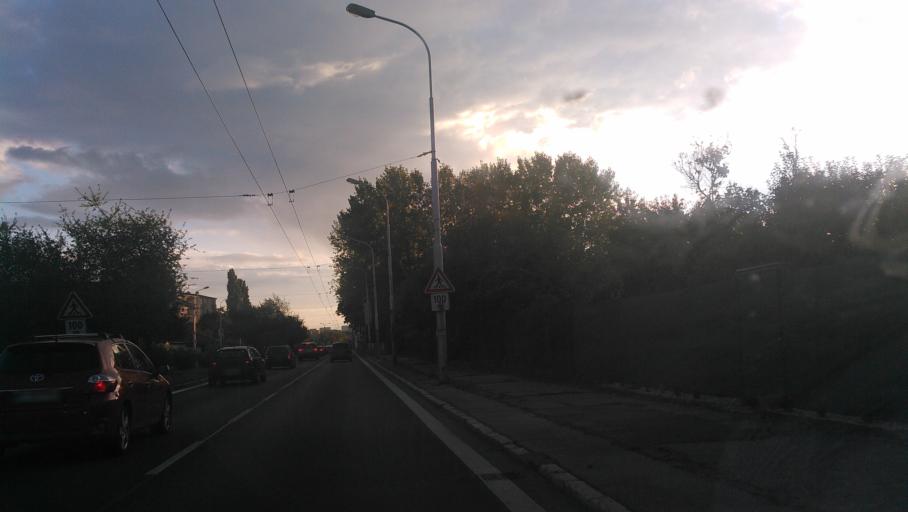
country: SK
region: Bratislavsky
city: Bratislava
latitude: 48.1727
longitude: 17.1615
